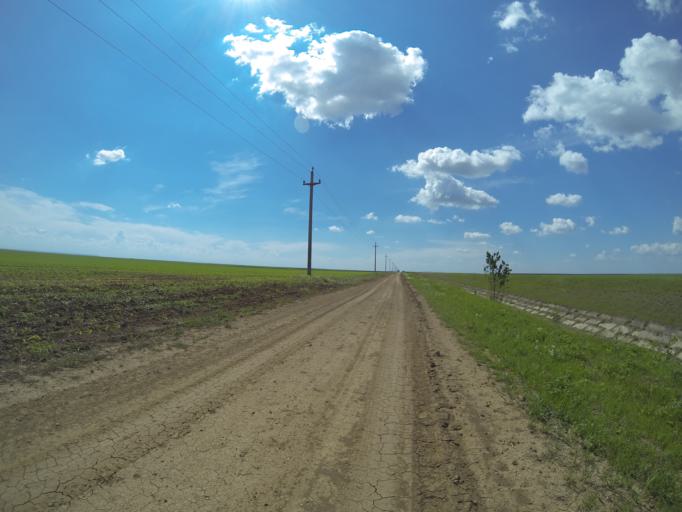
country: RO
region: Dolj
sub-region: Comuna Dranicu
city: Dranic
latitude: 44.0170
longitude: 23.7824
